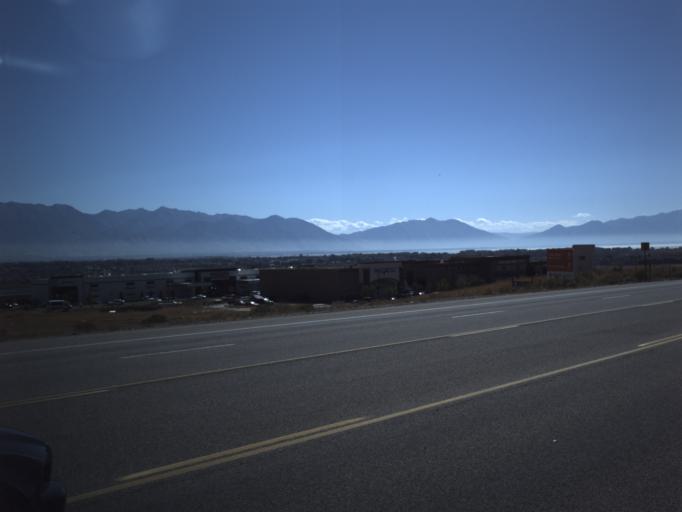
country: US
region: Utah
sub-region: Utah County
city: Saratoga Springs
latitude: 40.4032
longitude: -111.9204
